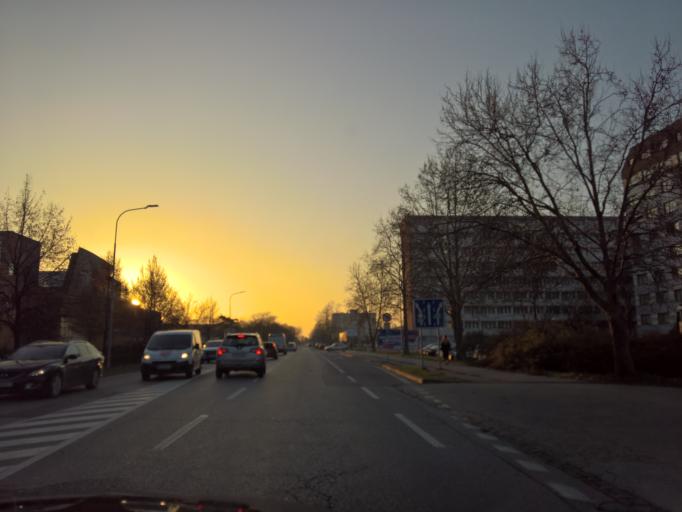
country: SK
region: Nitriansky
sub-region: Okres Nitra
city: Nitra
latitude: 48.3083
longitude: 18.0981
